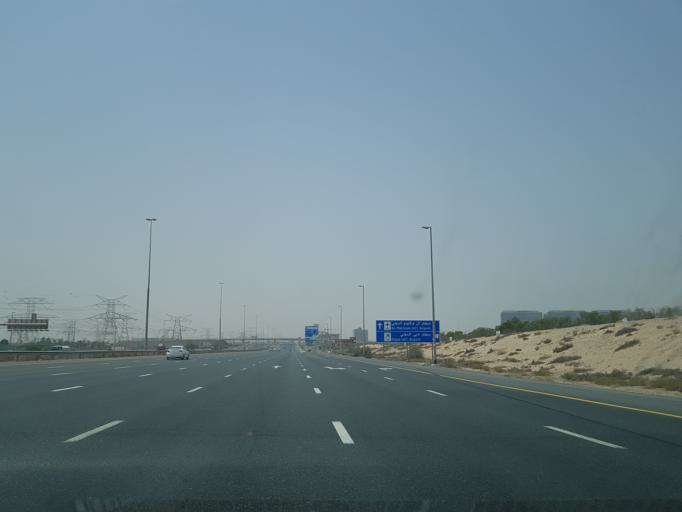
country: AE
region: Dubai
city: Dubai
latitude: 25.0934
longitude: 55.4006
